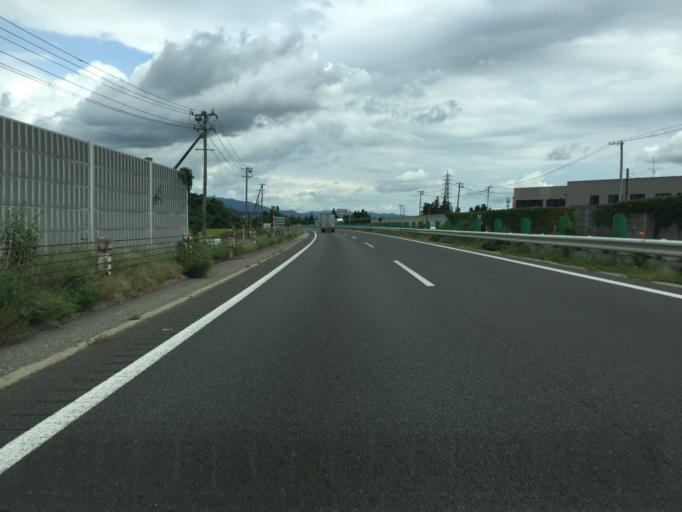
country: JP
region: Fukushima
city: Fukushima-shi
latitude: 37.8063
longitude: 140.4648
